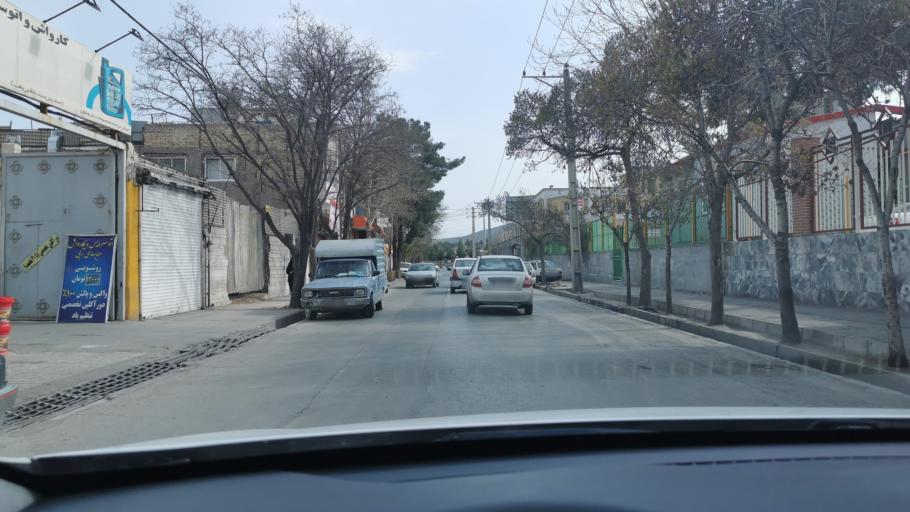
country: IR
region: Razavi Khorasan
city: Mashhad
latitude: 36.2740
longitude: 59.5689
